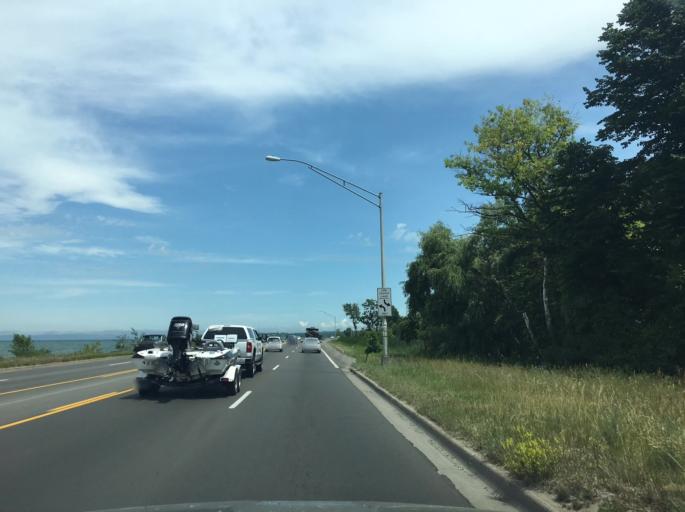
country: US
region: Michigan
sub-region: Grand Traverse County
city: Traverse City
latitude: 44.7523
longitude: -85.5224
